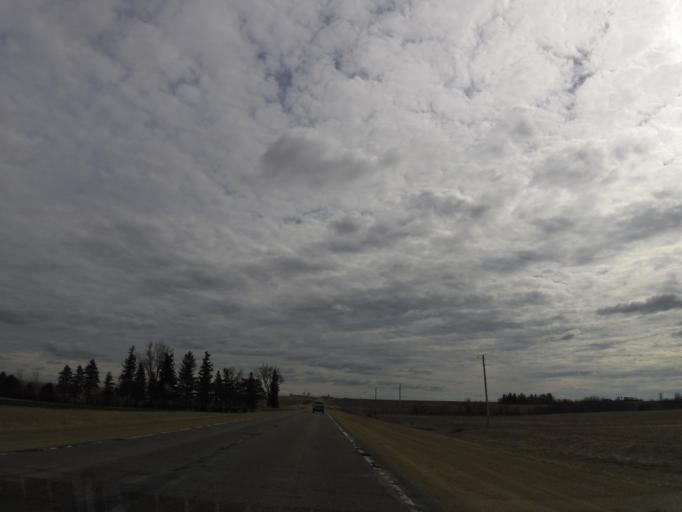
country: US
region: Iowa
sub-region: Howard County
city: Cresco
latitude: 43.3379
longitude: -92.2986
